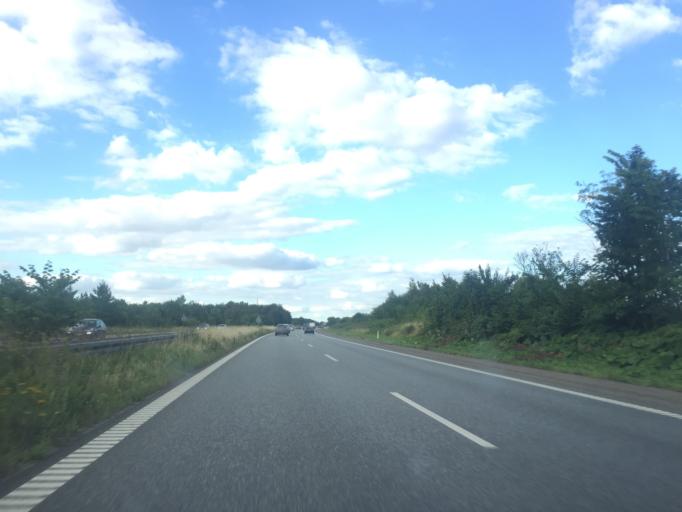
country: DK
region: Zealand
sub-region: Koge Kommune
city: Bjaeverskov
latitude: 55.3690
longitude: 12.0808
